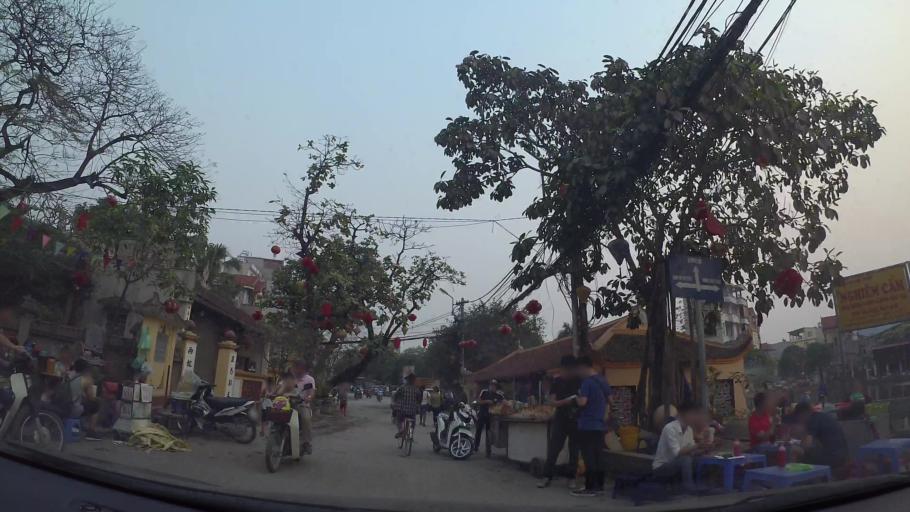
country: VN
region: Ha Noi
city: Thanh Xuan
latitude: 20.9805
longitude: 105.8009
